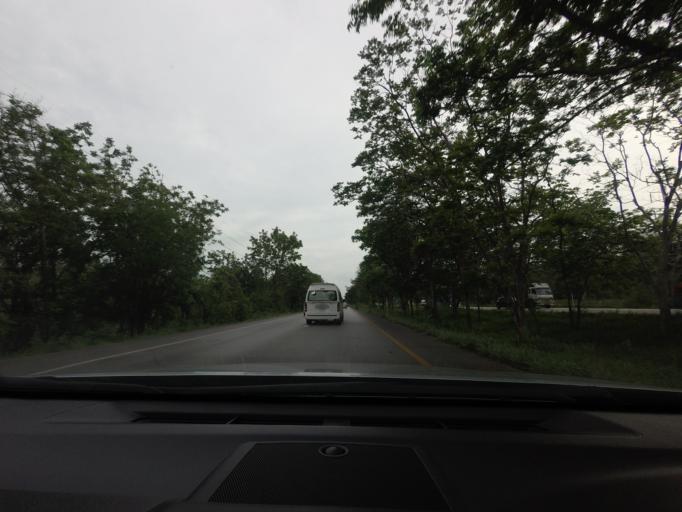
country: TH
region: Phetchaburi
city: Cha-am
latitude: 12.7034
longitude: 99.9097
